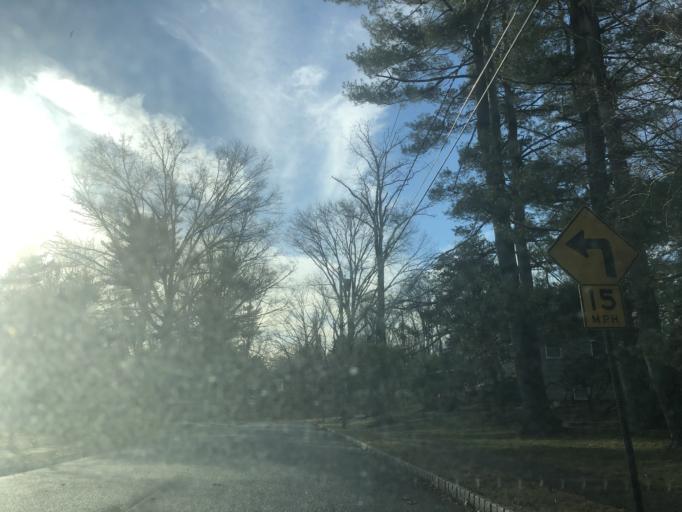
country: US
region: New Jersey
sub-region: Somerset County
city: Kingston
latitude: 40.3671
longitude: -74.6309
